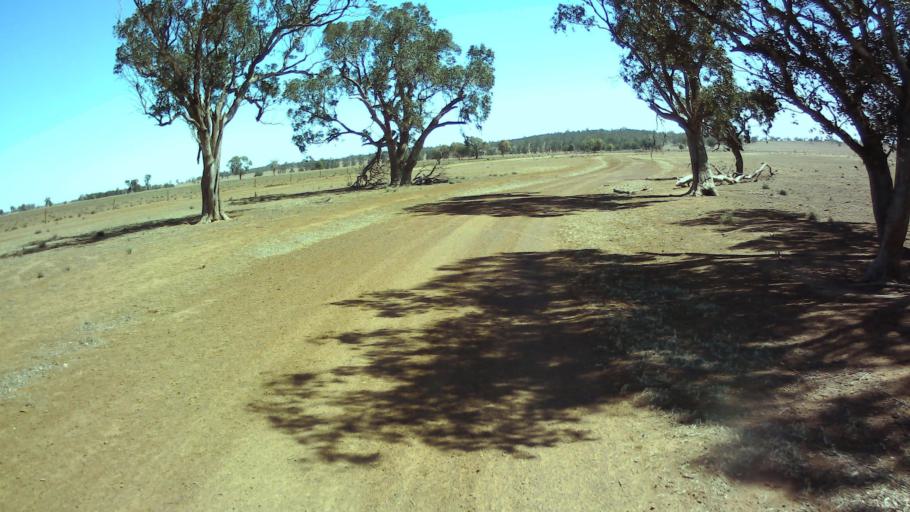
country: AU
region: New South Wales
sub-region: Forbes
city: Forbes
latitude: -33.6984
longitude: 147.6699
